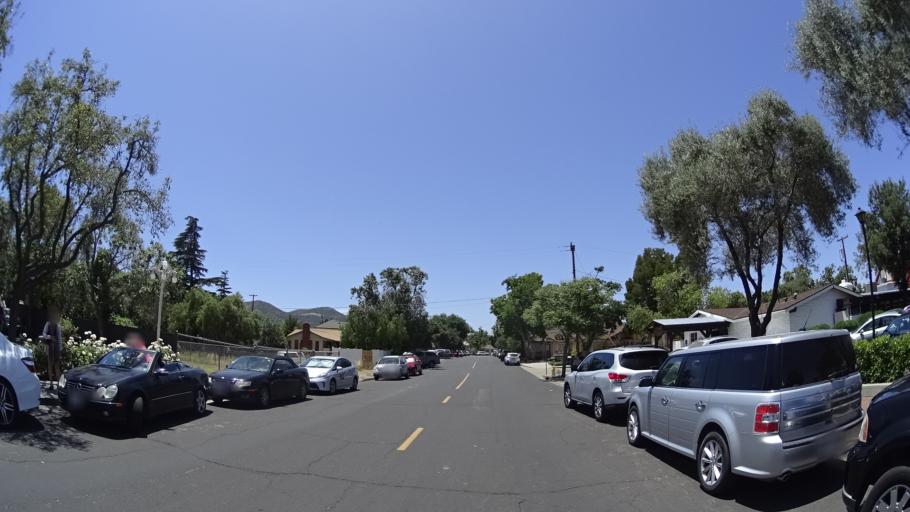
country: US
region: California
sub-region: Santa Barbara County
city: Solvang
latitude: 34.5952
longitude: -120.1435
